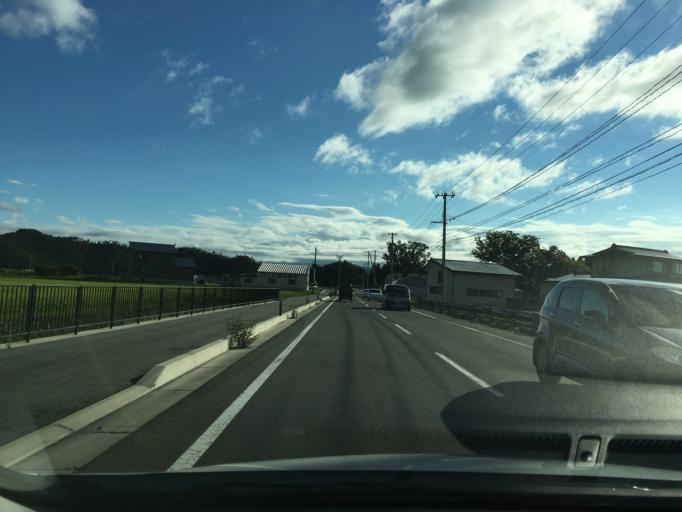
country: JP
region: Yamagata
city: Takahata
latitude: 37.9439
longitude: 140.1725
